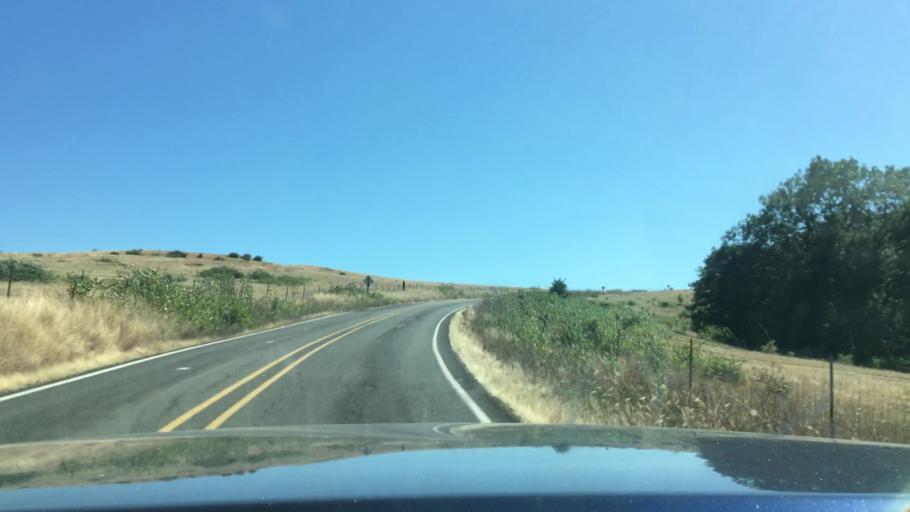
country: US
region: Oregon
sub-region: Douglas County
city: Winston
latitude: 43.1331
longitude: -123.4123
